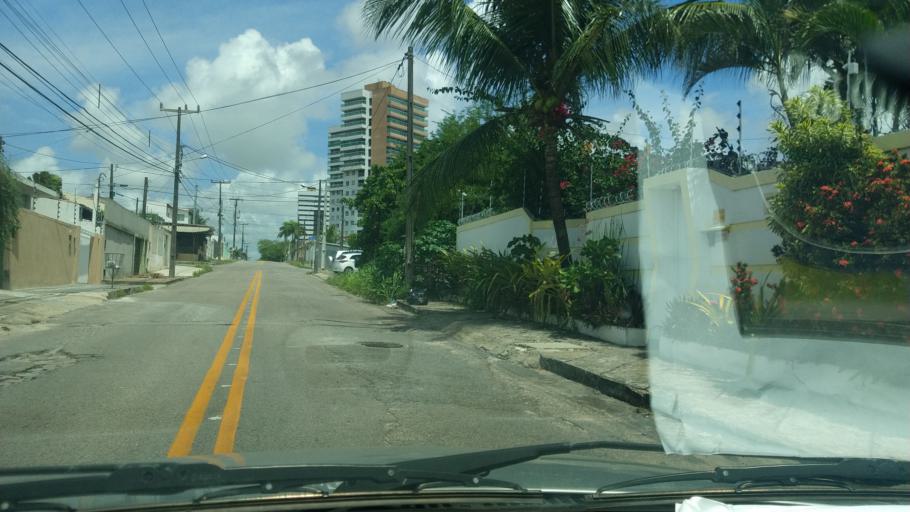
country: BR
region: Rio Grande do Norte
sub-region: Natal
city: Natal
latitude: -5.8658
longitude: -35.1986
